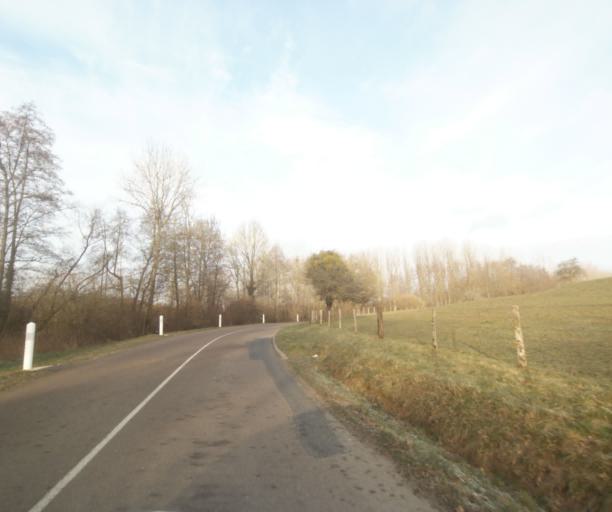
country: FR
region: Champagne-Ardenne
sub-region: Departement de la Marne
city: Sermaize-les-Bains
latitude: 48.7419
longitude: 4.9066
